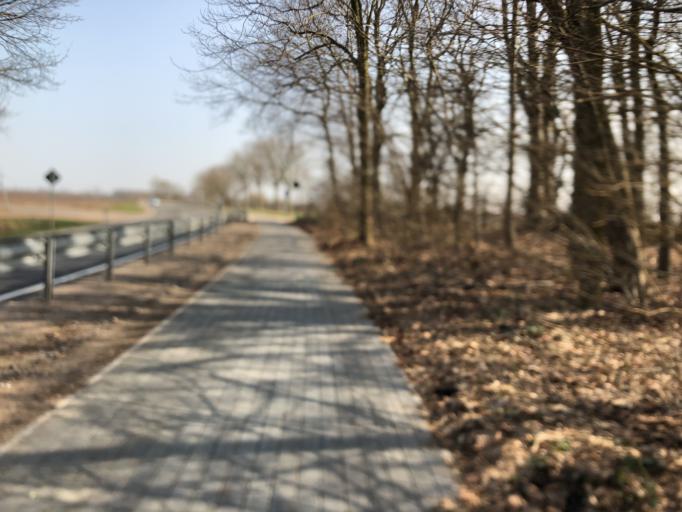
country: DE
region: Schleswig-Holstein
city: Jerrishoe
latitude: 54.6777
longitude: 9.3653
